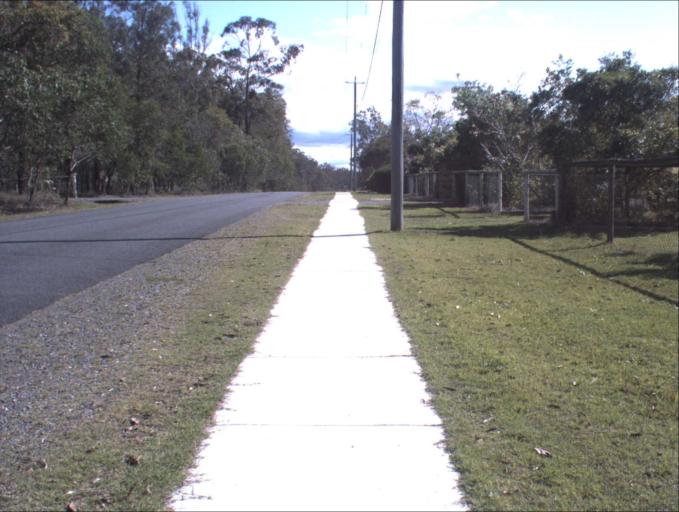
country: AU
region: Queensland
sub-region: Logan
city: Park Ridge South
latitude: -27.7437
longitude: 153.0420
